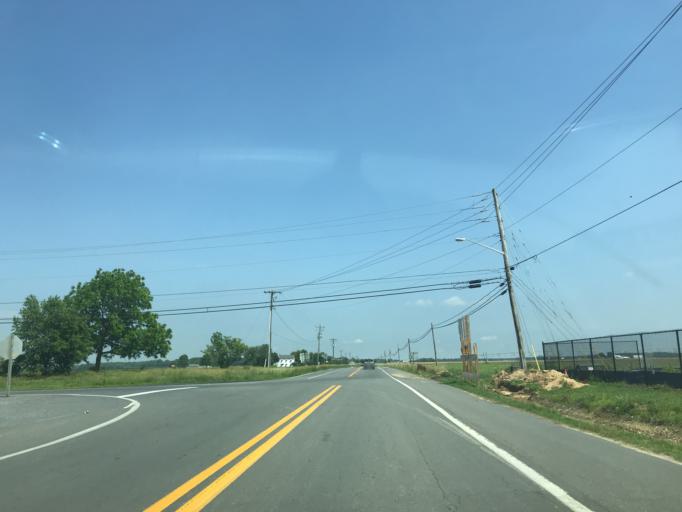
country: US
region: Maryland
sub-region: Dorchester County
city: Hurlock
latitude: 38.5889
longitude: -75.8716
